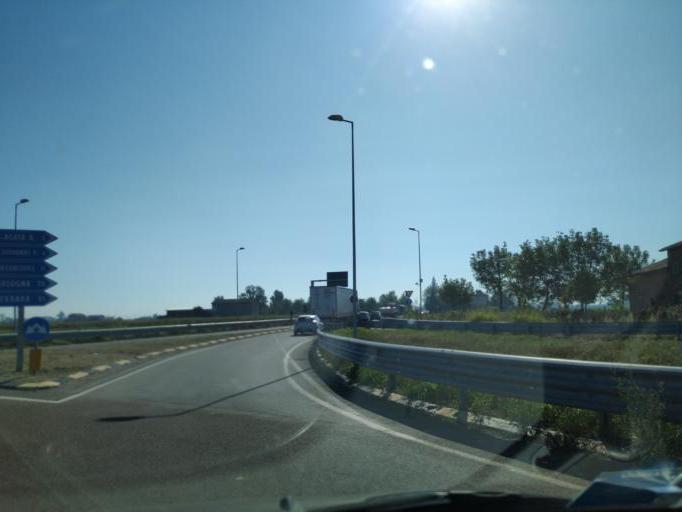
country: IT
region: Emilia-Romagna
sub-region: Provincia di Modena
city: Nonantola
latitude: 44.6729
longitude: 11.0834
